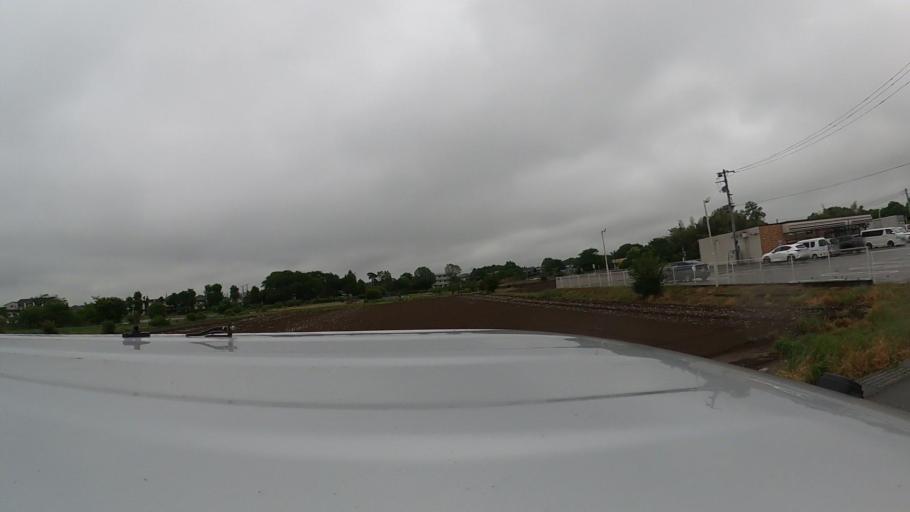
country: JP
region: Ibaraki
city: Ushiku
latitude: 36.0197
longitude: 140.0999
